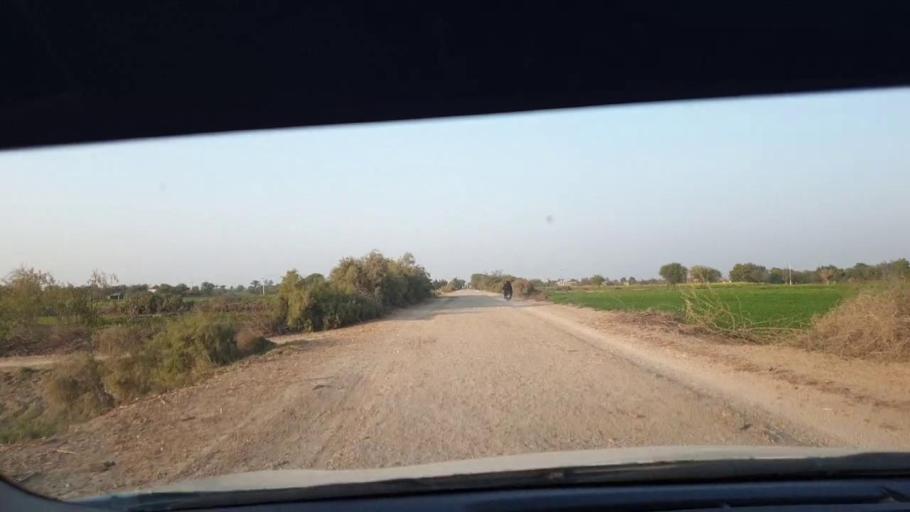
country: PK
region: Sindh
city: Berani
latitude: 25.8485
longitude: 68.8166
